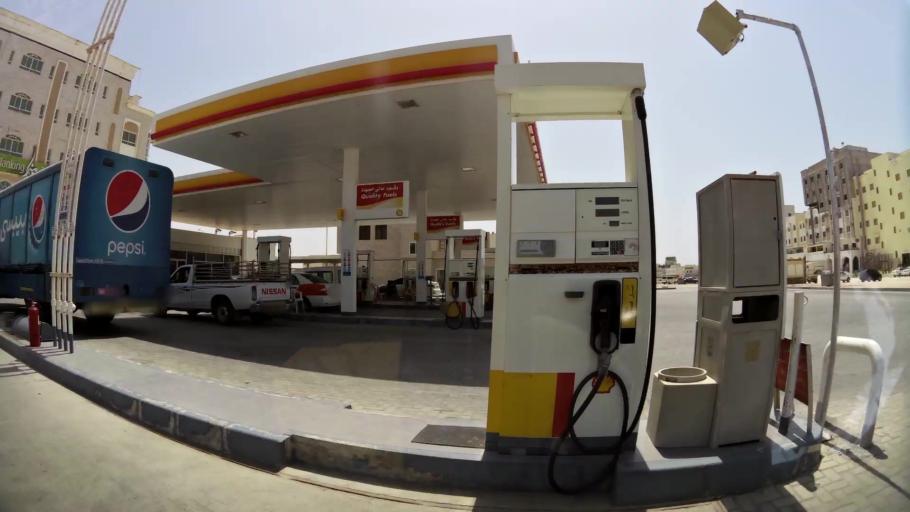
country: OM
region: Zufar
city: Salalah
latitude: 17.0187
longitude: 54.1011
